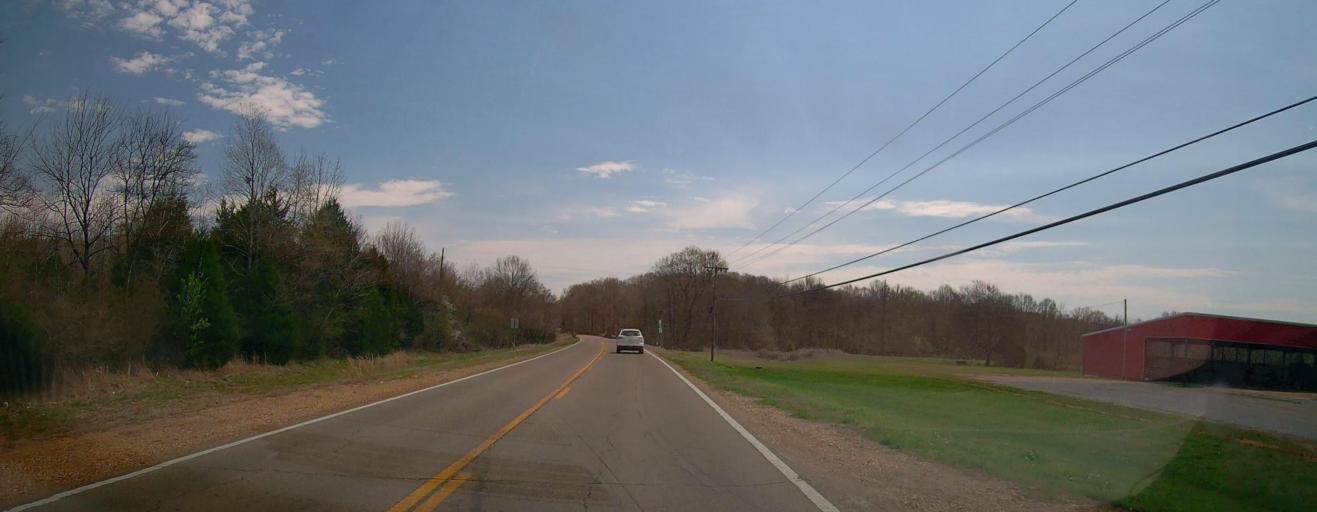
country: US
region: Mississippi
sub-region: Union County
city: New Albany
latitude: 34.4711
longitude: -88.9914
